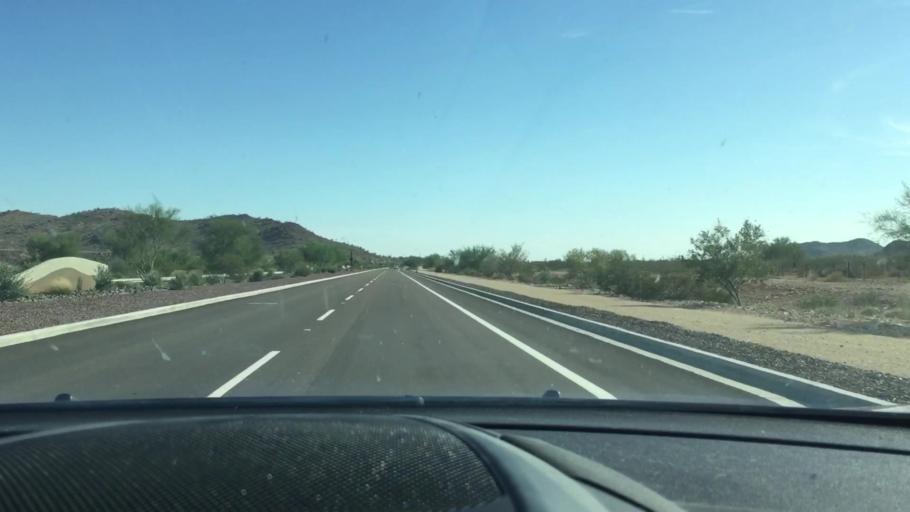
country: US
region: Arizona
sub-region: Maricopa County
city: Sun City West
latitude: 33.7597
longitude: -112.2523
